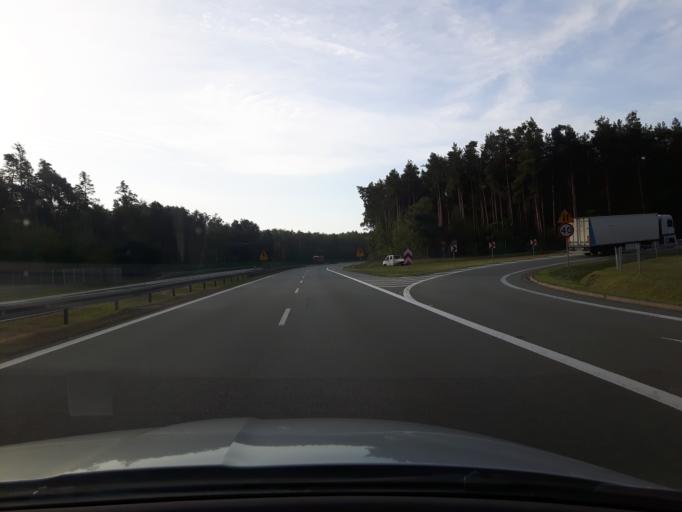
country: PL
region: Masovian Voivodeship
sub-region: Powiat bialobrzeski
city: Bialobrzegi
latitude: 51.6492
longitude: 20.9723
